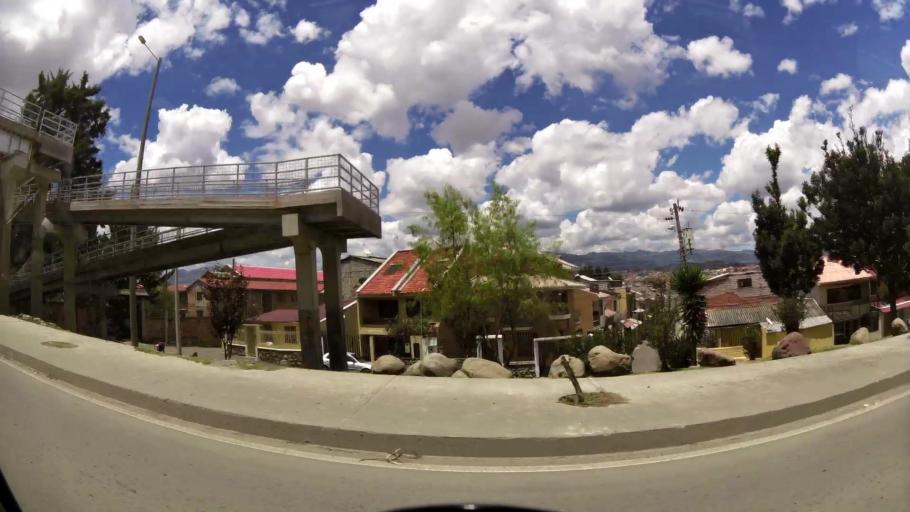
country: EC
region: Azuay
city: Cuenca
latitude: -2.9033
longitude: -78.9761
